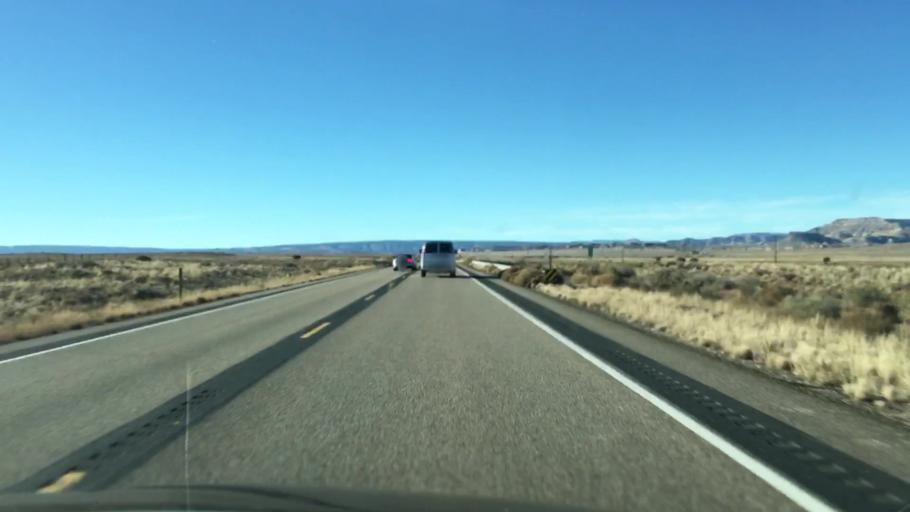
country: US
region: Arizona
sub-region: Coconino County
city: Page
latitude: 37.0980
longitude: -111.7801
